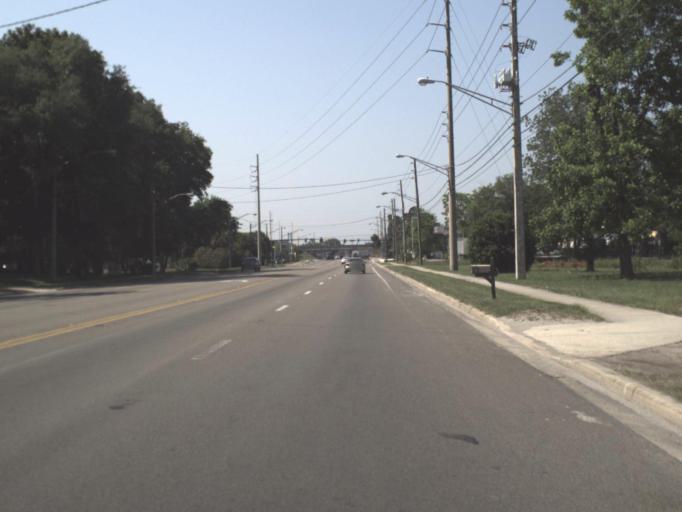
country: US
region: Florida
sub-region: Duval County
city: Jacksonville
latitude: 30.3199
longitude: -81.7521
